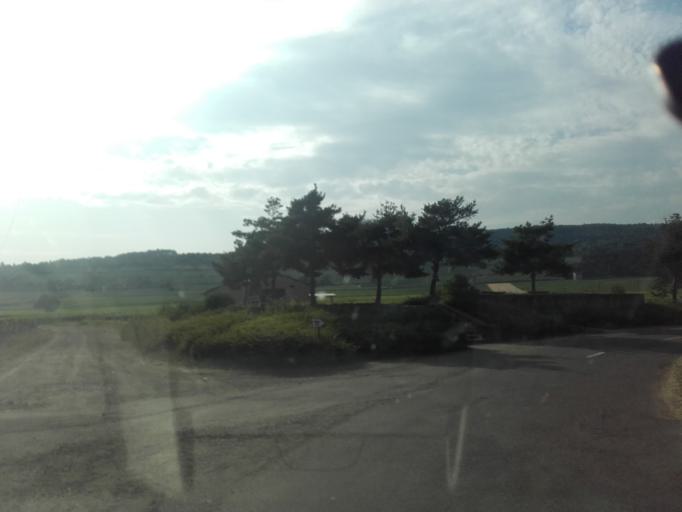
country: FR
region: Bourgogne
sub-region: Departement de la Cote-d'Or
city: Corpeau
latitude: 46.9494
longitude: 4.7515
